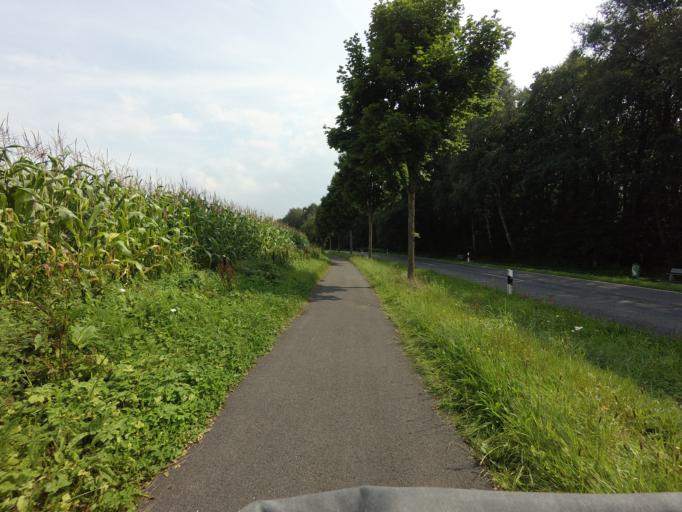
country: DE
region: Lower Saxony
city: Uelsen
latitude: 52.4721
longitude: 6.9057
